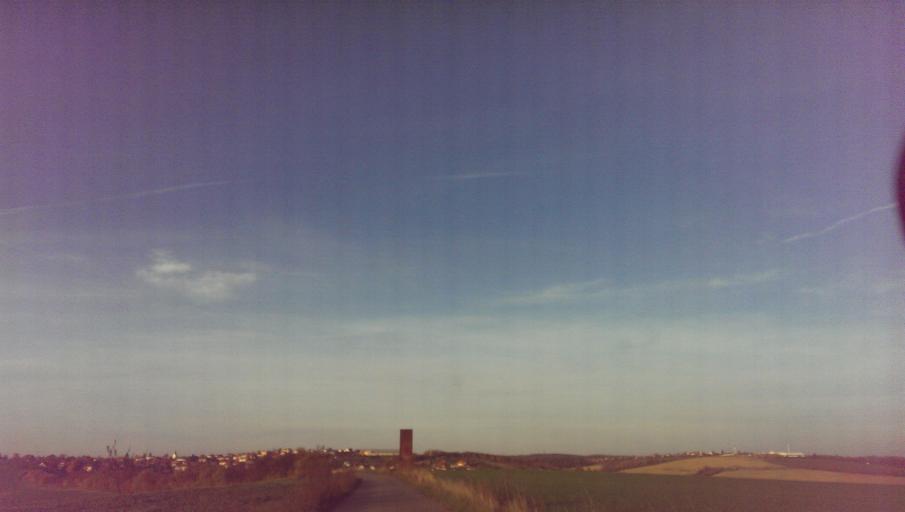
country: CZ
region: Zlin
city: Brezolupy
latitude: 49.1586
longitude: 17.6028
